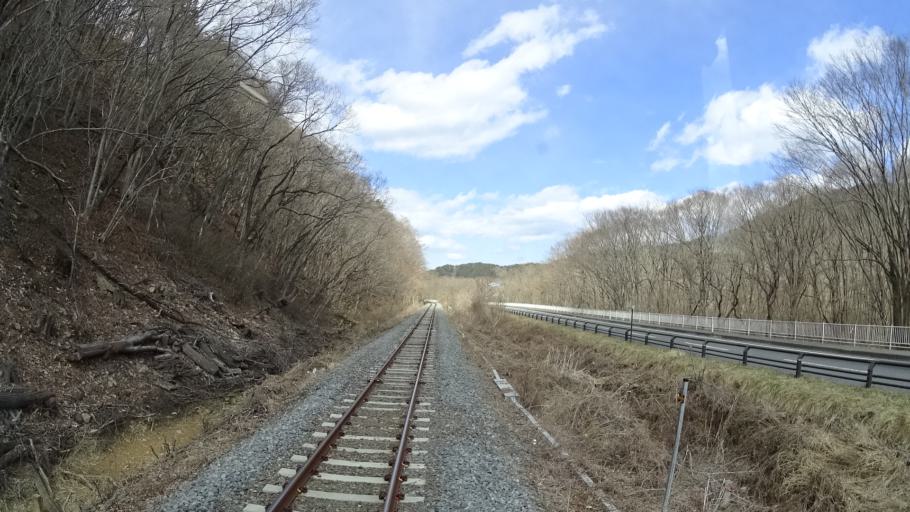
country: JP
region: Iwate
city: Yamada
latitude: 39.5503
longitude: 141.9392
